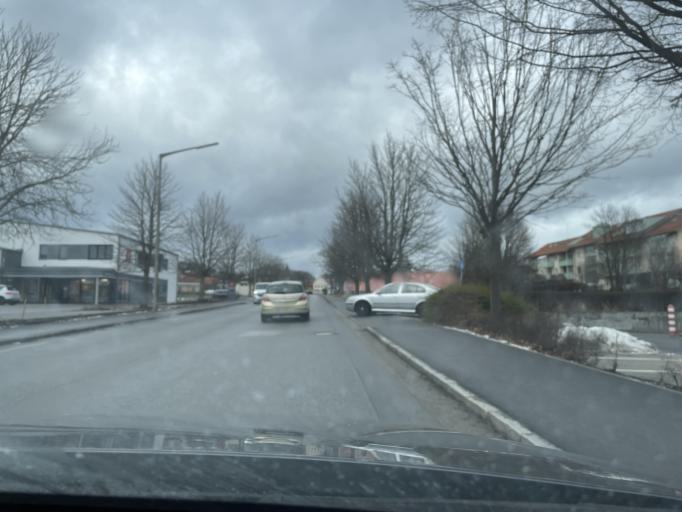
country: DE
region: Bavaria
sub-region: Upper Palatinate
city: Furth im Wald
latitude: 49.3063
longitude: 12.8343
